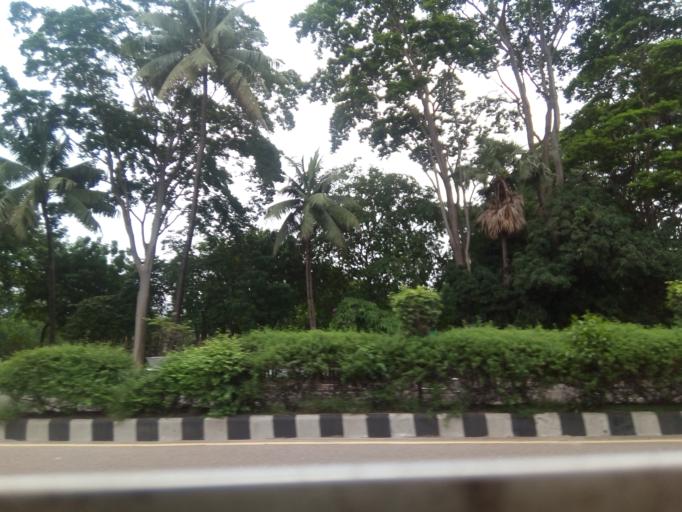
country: BD
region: Dhaka
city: Azimpur
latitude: 23.7672
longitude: 90.3889
